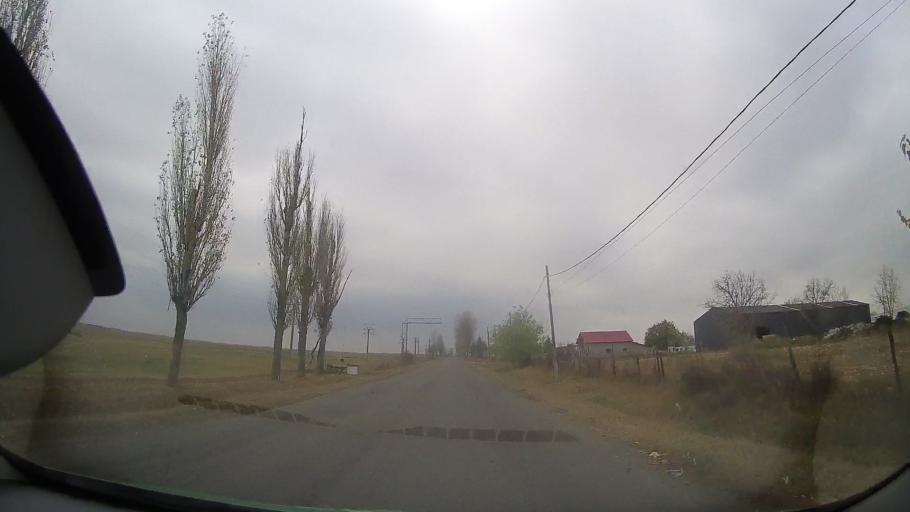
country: RO
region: Buzau
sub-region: Comuna Pogoanele
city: Pogoanele
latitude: 44.9020
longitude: 26.9776
